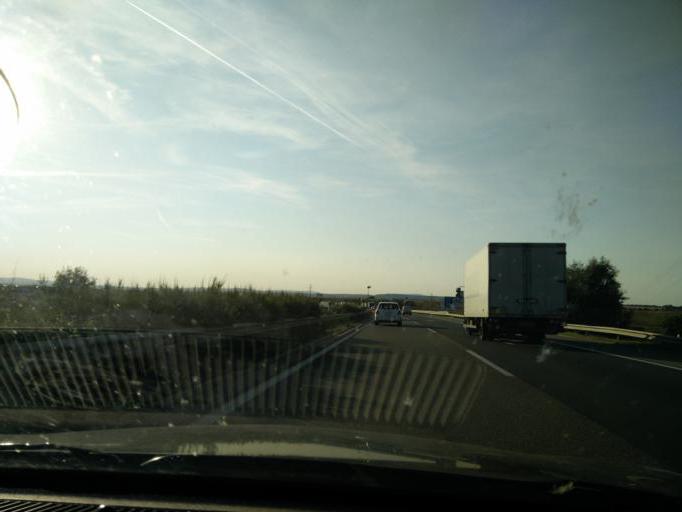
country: HU
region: Pest
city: Biatorbagy
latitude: 47.4917
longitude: 18.8262
